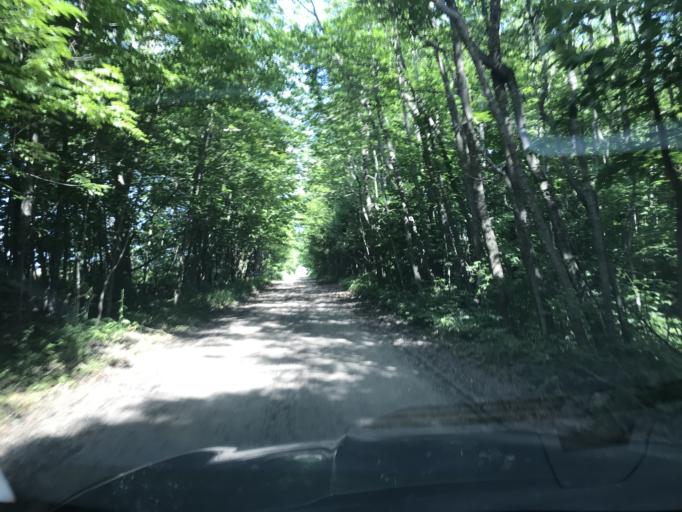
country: US
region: Michigan
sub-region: Cheboygan County
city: Cheboygan
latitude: 45.6216
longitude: -84.6751
